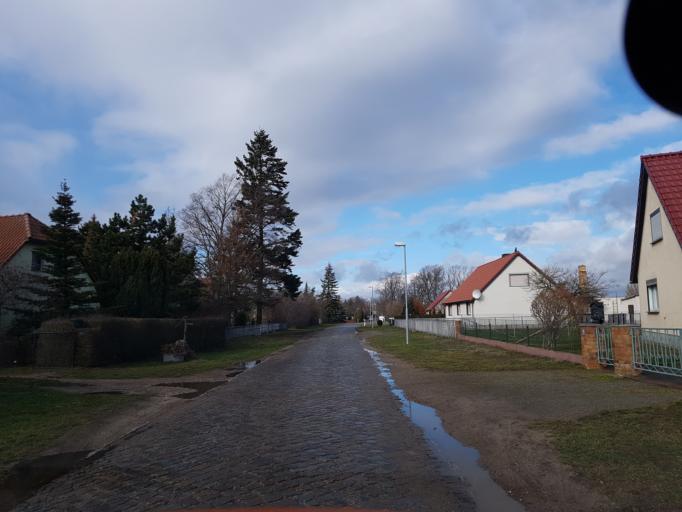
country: DE
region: Brandenburg
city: Muhlberg
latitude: 51.4783
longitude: 13.1977
